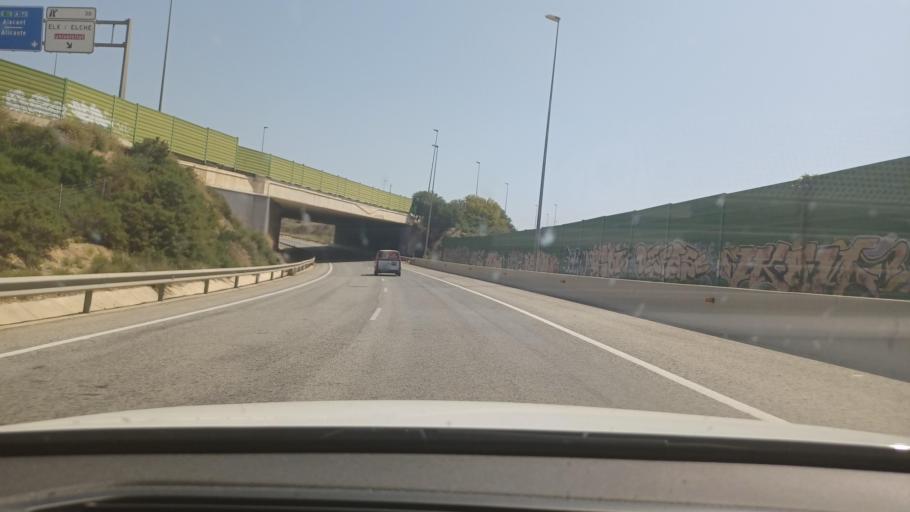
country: ES
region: Valencia
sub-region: Provincia de Alicante
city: Elche
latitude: 38.2976
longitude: -0.6728
